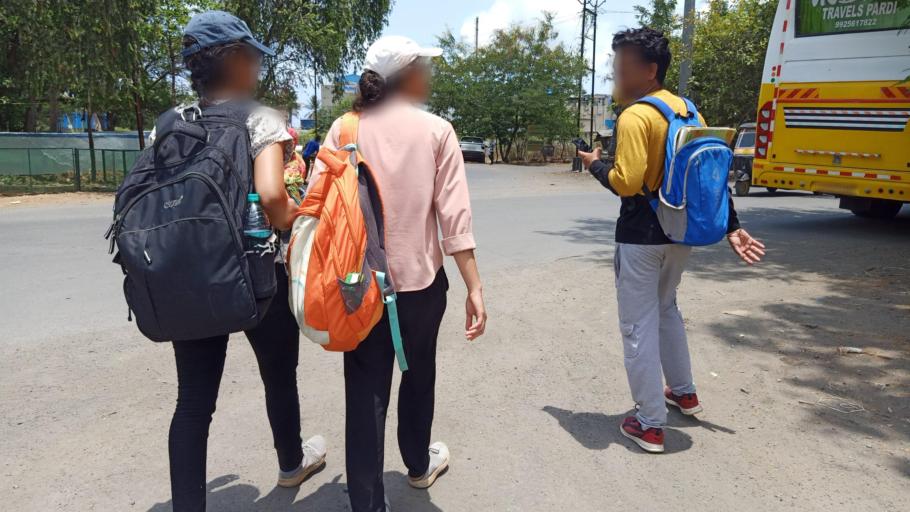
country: IN
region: Gujarat
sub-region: Valsad
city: Vapi
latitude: 20.2991
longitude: 72.8488
